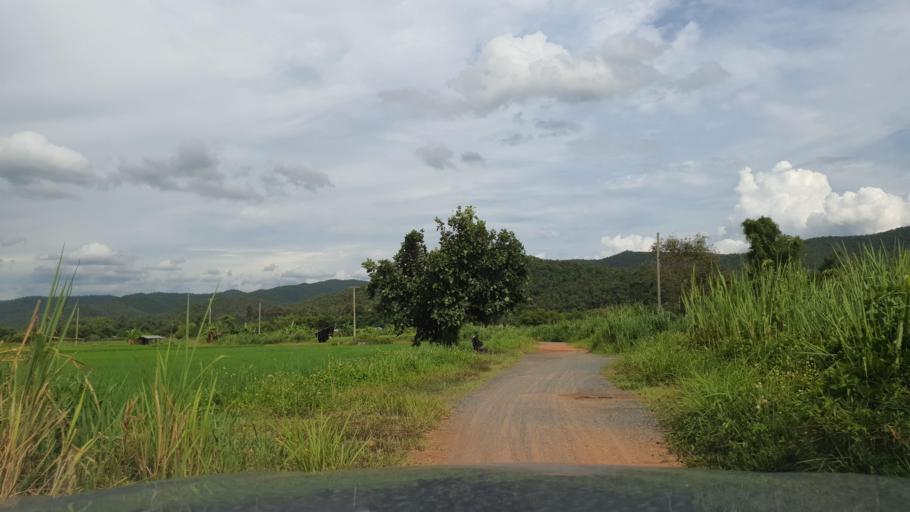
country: TH
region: Chiang Mai
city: Mae On
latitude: 18.7817
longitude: 99.1852
